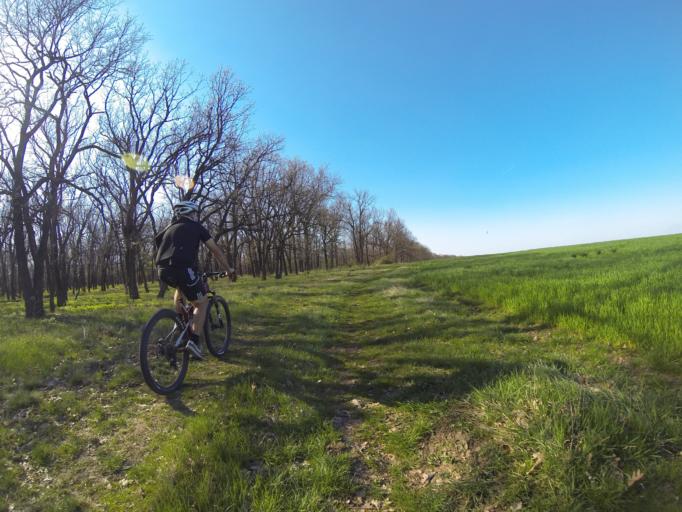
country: RO
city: Varvoru
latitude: 44.2310
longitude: 23.6732
